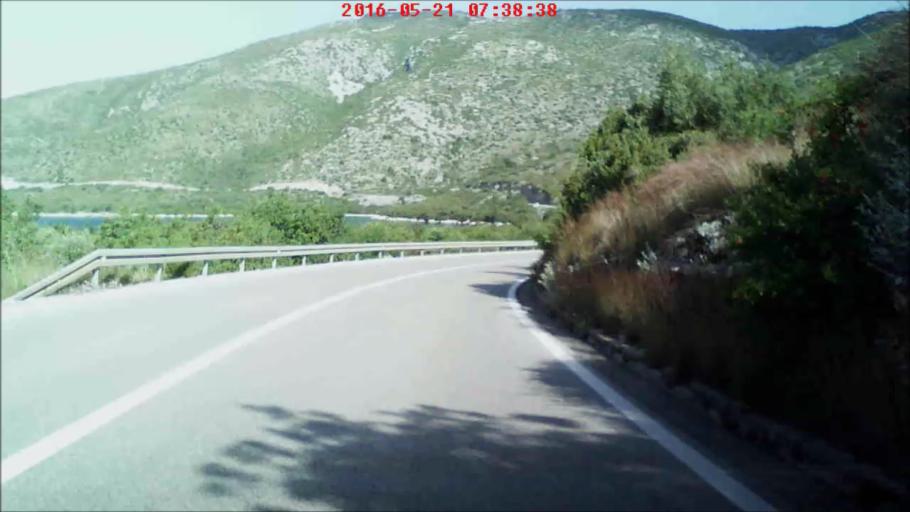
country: HR
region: Dubrovacko-Neretvanska
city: Podgora
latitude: 42.8015
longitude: 17.8486
